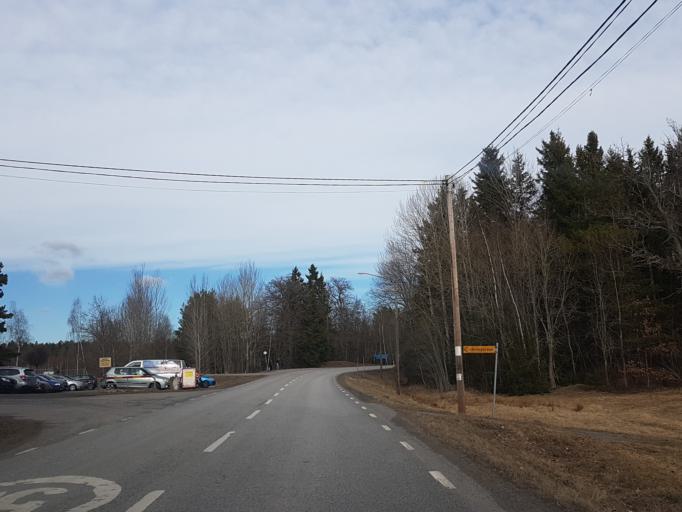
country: SE
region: Stockholm
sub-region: Norrtalje Kommun
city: Norrtalje
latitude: 59.6808
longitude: 18.7484
